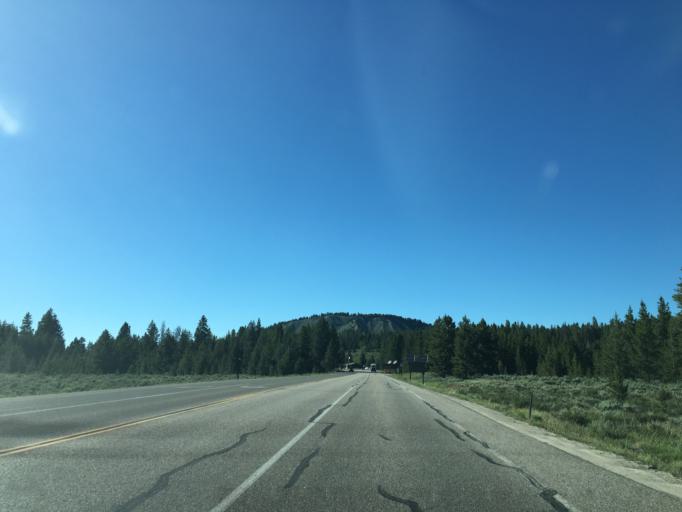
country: US
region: Wyoming
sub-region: Teton County
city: Jackson
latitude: 43.8405
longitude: -110.5102
